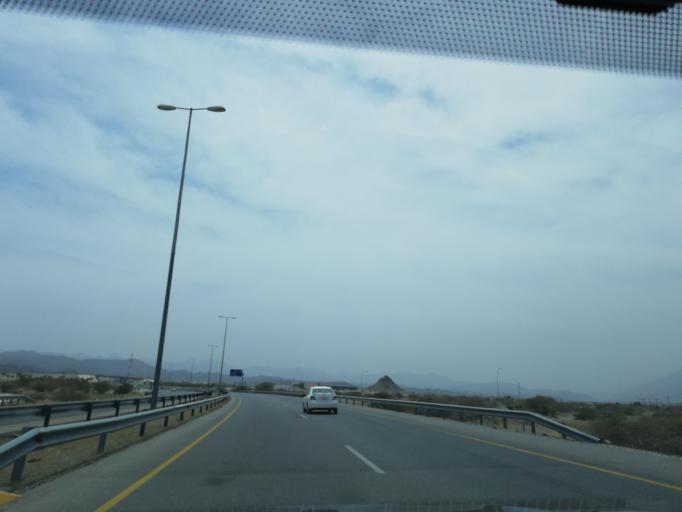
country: OM
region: Muhafazat ad Dakhiliyah
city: Sufalat Sama'il
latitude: 23.2855
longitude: 57.9356
